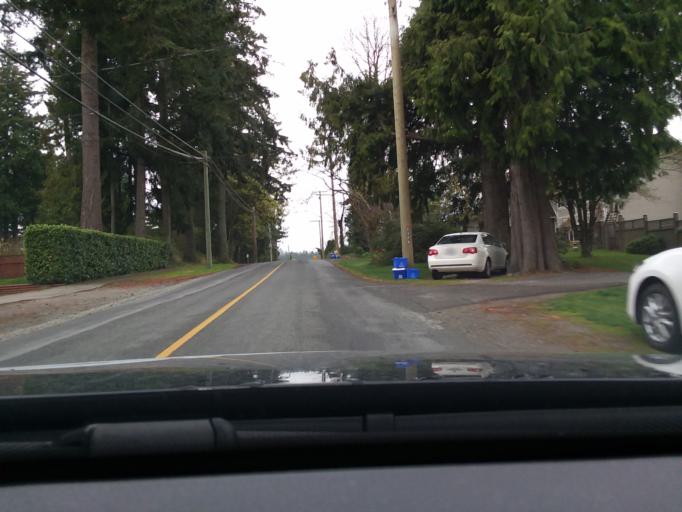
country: CA
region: British Columbia
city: North Saanich
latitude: 48.5544
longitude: -123.3993
